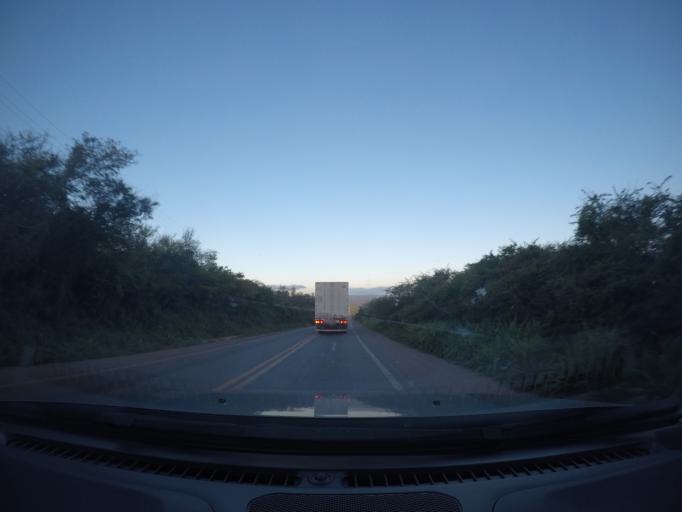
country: BR
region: Bahia
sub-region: Seabra
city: Seabra
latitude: -12.4135
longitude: -41.9775
